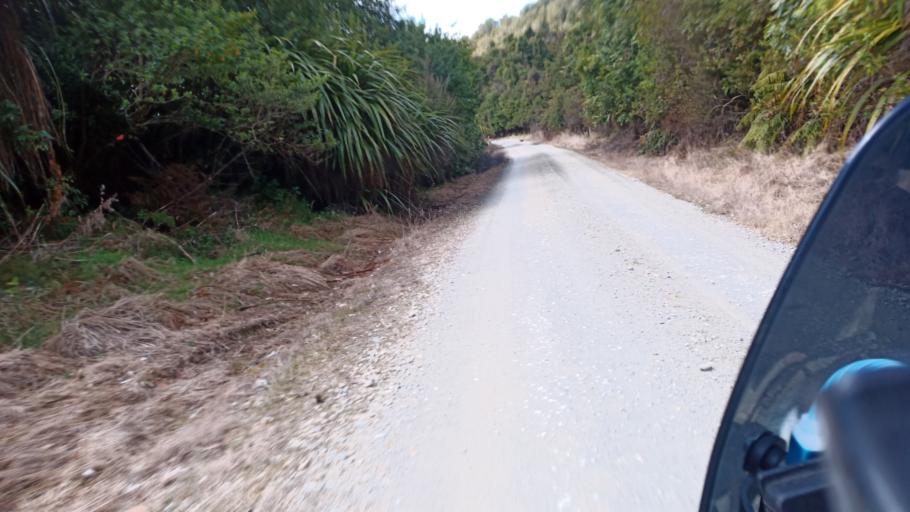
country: NZ
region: Gisborne
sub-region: Gisborne District
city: Gisborne
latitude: -38.8507
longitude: 177.7876
